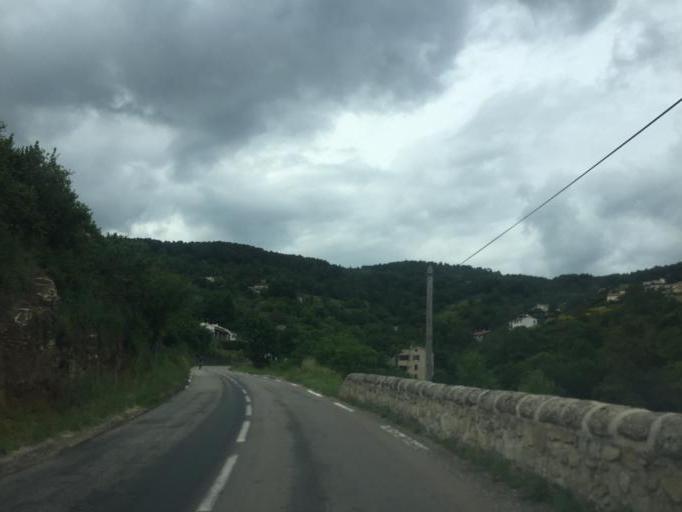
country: FR
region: Rhone-Alpes
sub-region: Departement de l'Ardeche
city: Privas
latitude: 44.7419
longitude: 4.6054
